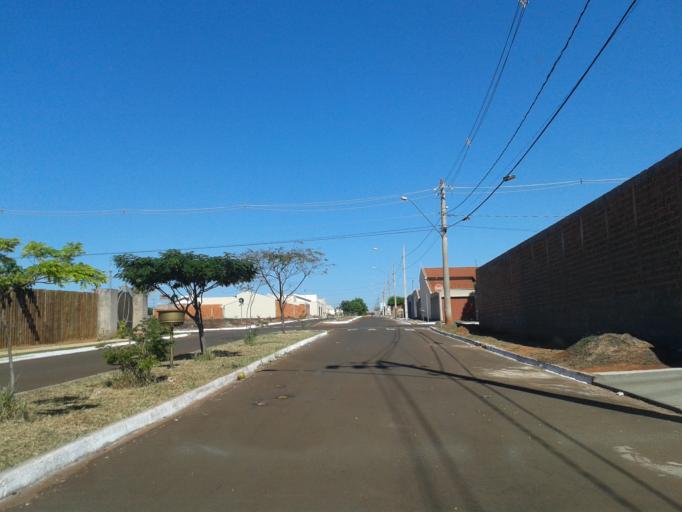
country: BR
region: Minas Gerais
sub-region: Santa Vitoria
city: Santa Vitoria
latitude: -18.8509
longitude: -50.1222
